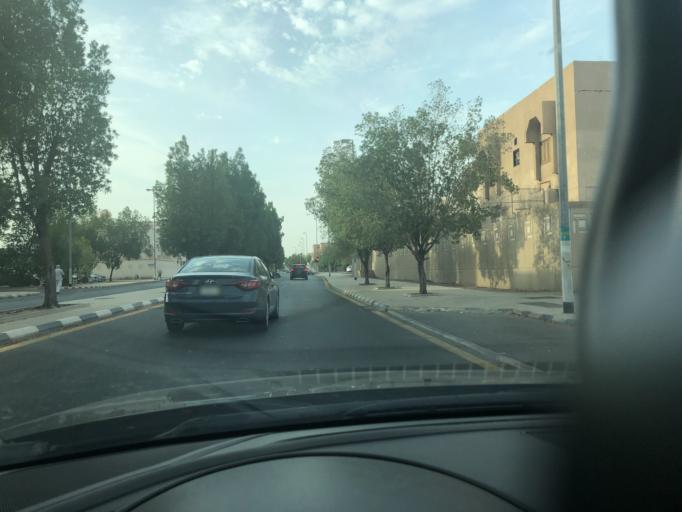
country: SA
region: Makkah
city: Mecca
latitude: 21.4091
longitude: 39.7804
